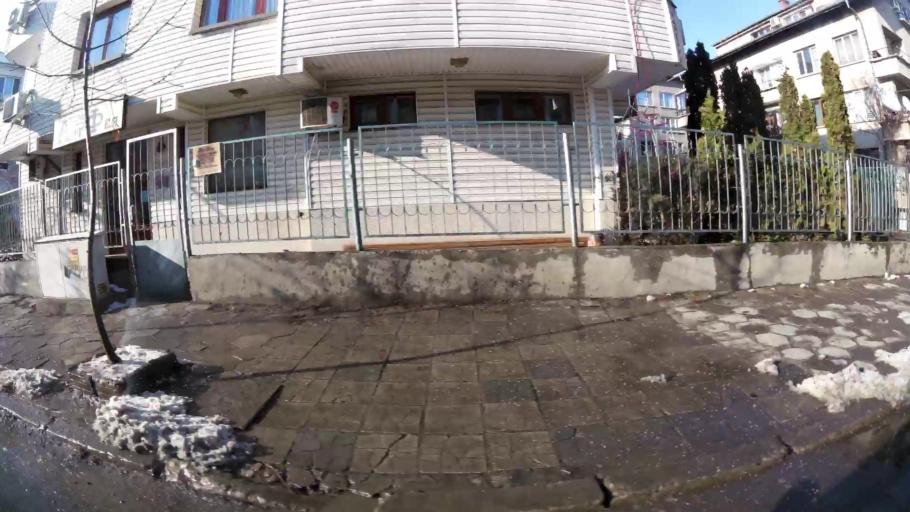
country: BG
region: Sofia-Capital
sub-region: Stolichna Obshtina
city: Sofia
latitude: 42.6689
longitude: 23.3620
